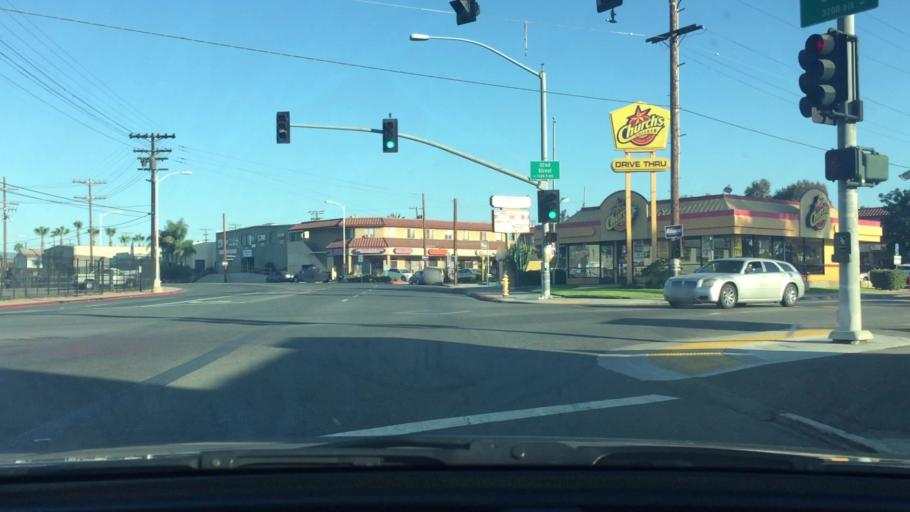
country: US
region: California
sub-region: San Diego County
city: National City
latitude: 32.6924
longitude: -117.1253
